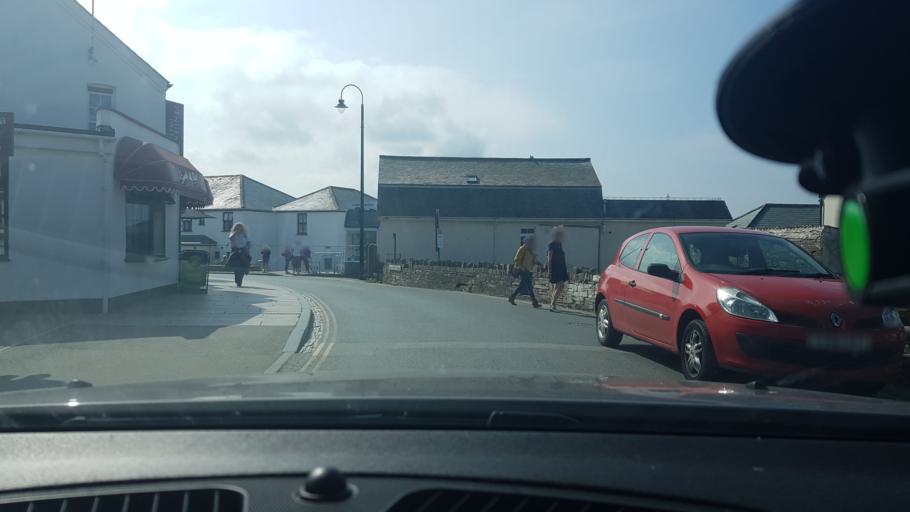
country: GB
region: England
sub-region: Cornwall
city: Tintagel
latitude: 50.6647
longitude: -4.7535
